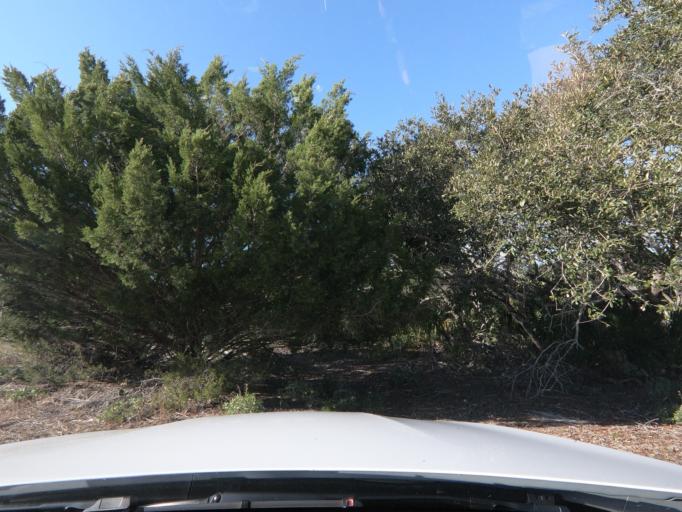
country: US
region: Florida
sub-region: Bay County
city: Lower Grand Lagoon
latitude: 30.1347
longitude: -85.7434
